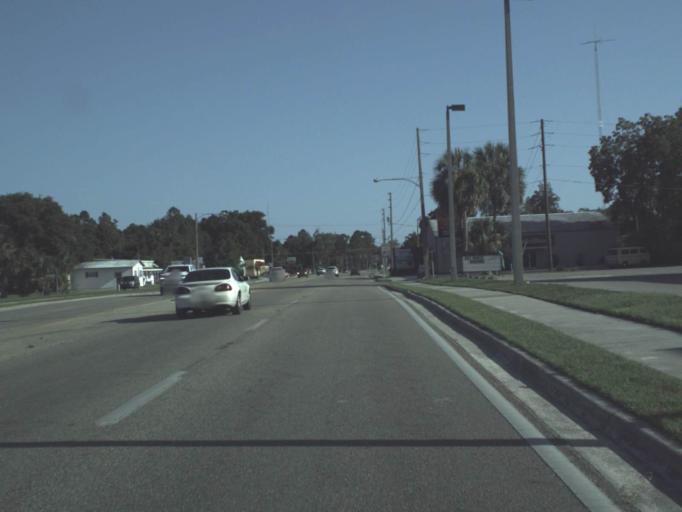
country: US
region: Florida
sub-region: Taylor County
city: Perry
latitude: 30.1094
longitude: -83.5822
